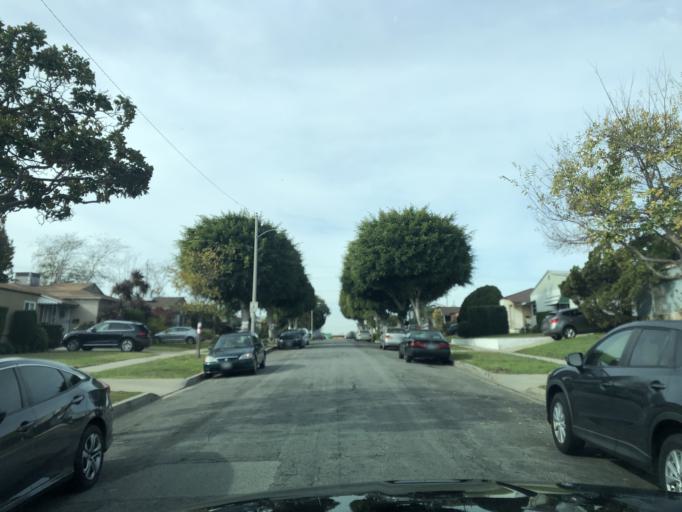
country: US
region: California
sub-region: Los Angeles County
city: Ladera Heights
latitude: 33.9789
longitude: -118.3678
